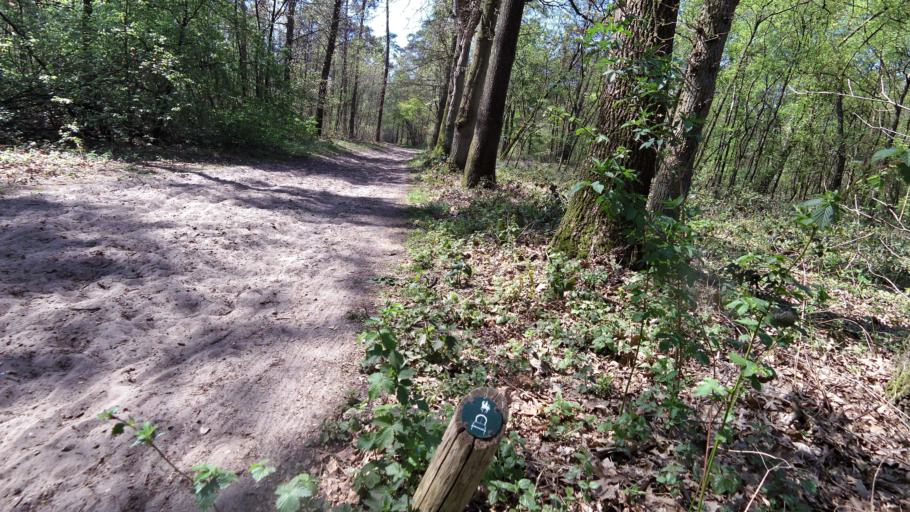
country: NL
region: Gelderland
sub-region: Gemeente Arnhem
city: Hoogkamp
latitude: 52.0289
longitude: 5.8675
